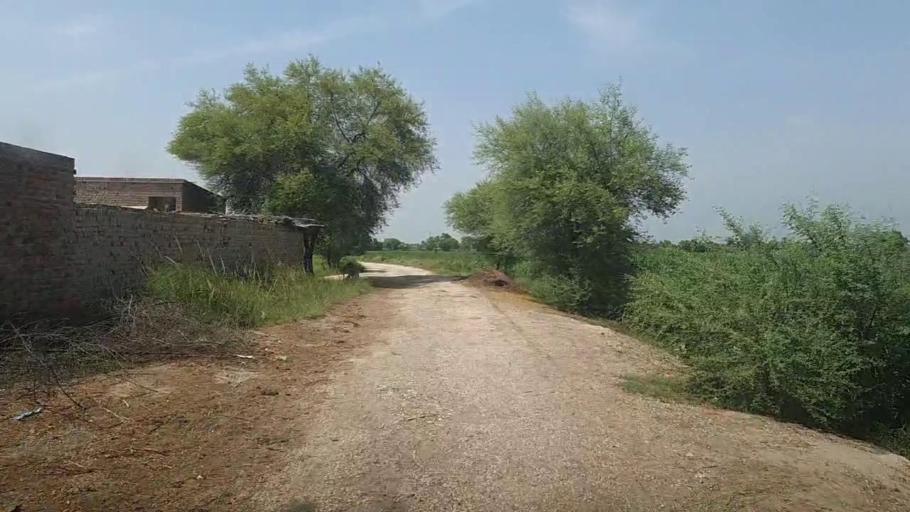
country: PK
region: Sindh
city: Ubauro
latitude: 28.1717
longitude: 69.8159
